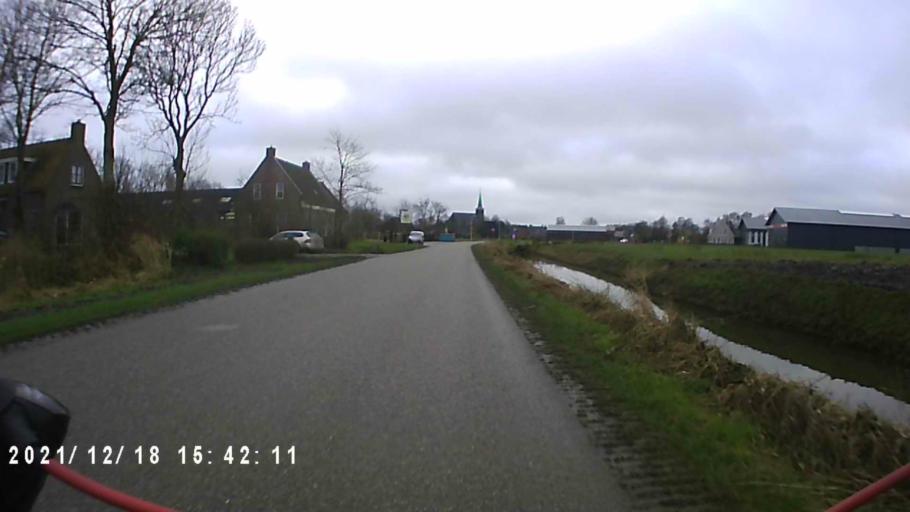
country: NL
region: Friesland
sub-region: Gemeente Dongeradeel
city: Anjum
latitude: 53.3336
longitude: 6.1048
